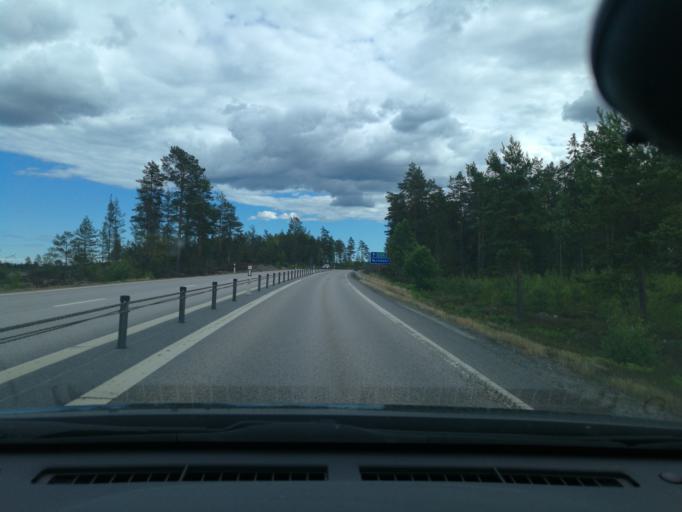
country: SE
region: Kalmar
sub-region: Vasterviks Kommun
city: Forserum
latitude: 58.0626
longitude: 16.5272
